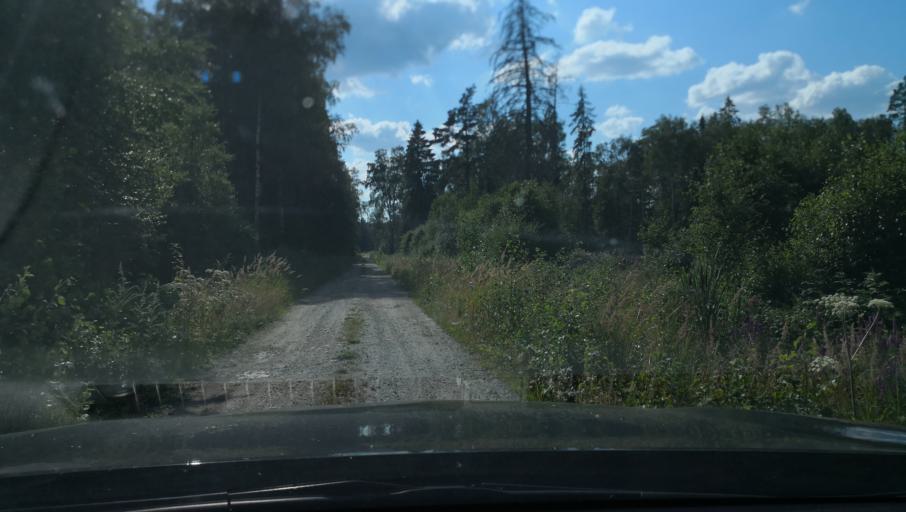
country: SE
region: Vaestmanland
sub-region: Vasteras
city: Skultuna
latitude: 59.7252
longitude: 16.3610
